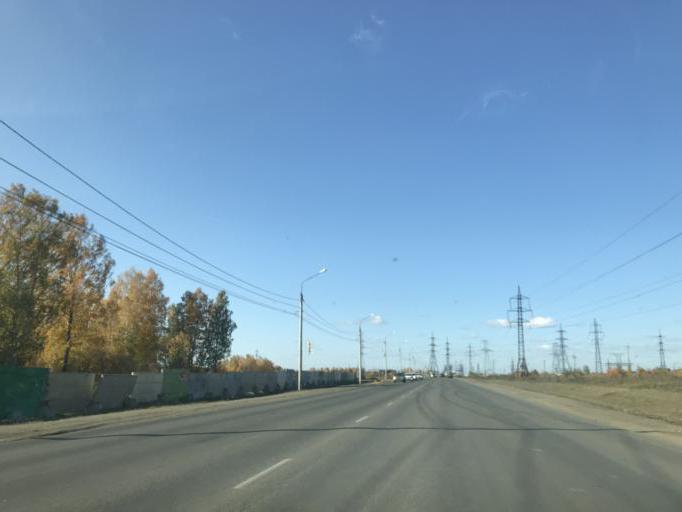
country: RU
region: Chelyabinsk
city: Roshchino
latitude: 55.2214
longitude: 61.2956
